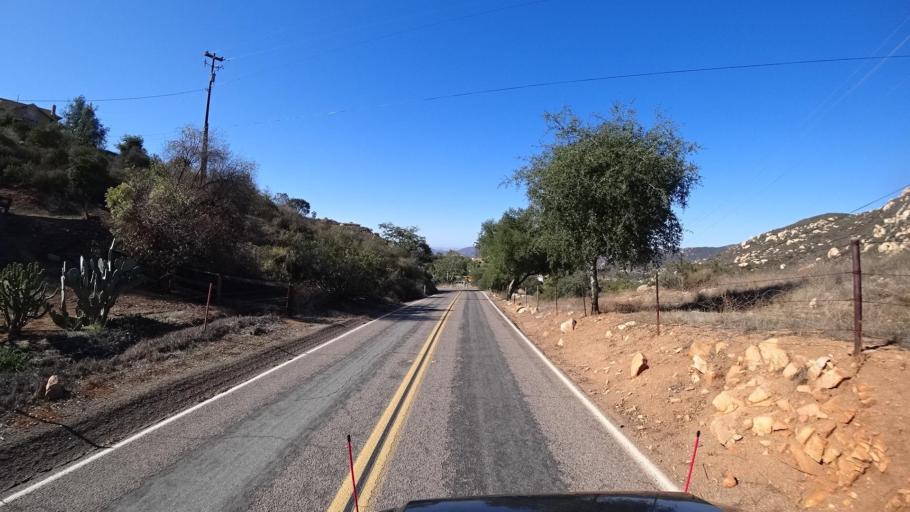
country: US
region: California
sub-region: San Diego County
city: Jamul
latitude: 32.7105
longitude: -116.7829
